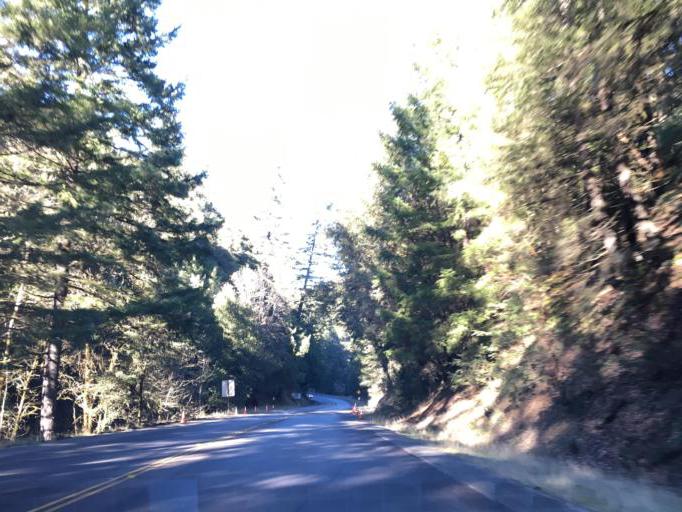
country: US
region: California
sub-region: Mendocino County
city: Laytonville
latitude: 39.7946
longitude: -123.5426
